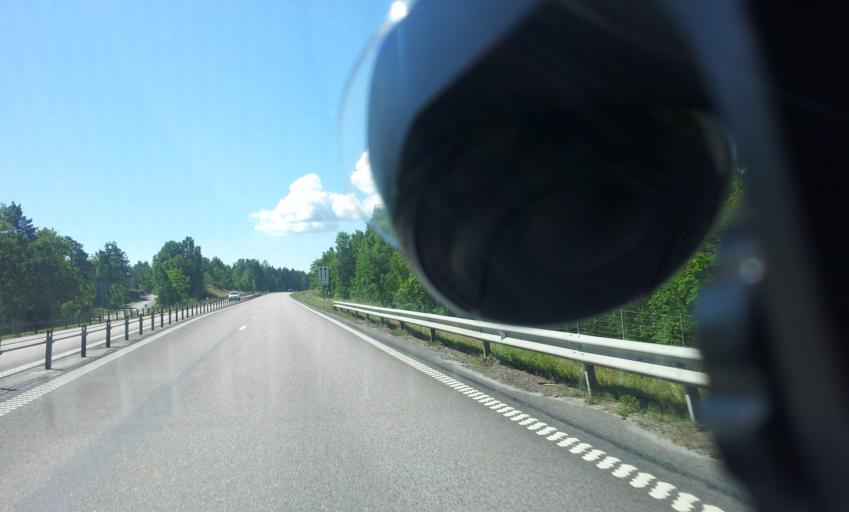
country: SE
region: Kalmar
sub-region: Oskarshamns Kommun
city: Paskallavik
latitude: 57.2092
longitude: 16.4357
